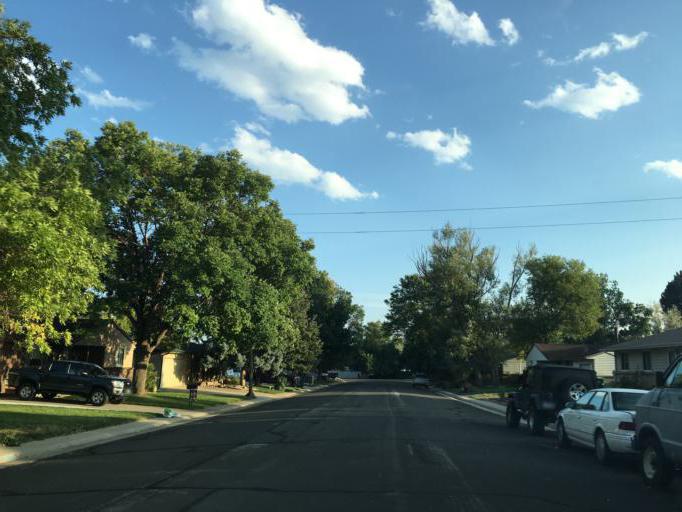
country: US
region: Colorado
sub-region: Jefferson County
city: Applewood
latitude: 39.7924
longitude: -105.1474
